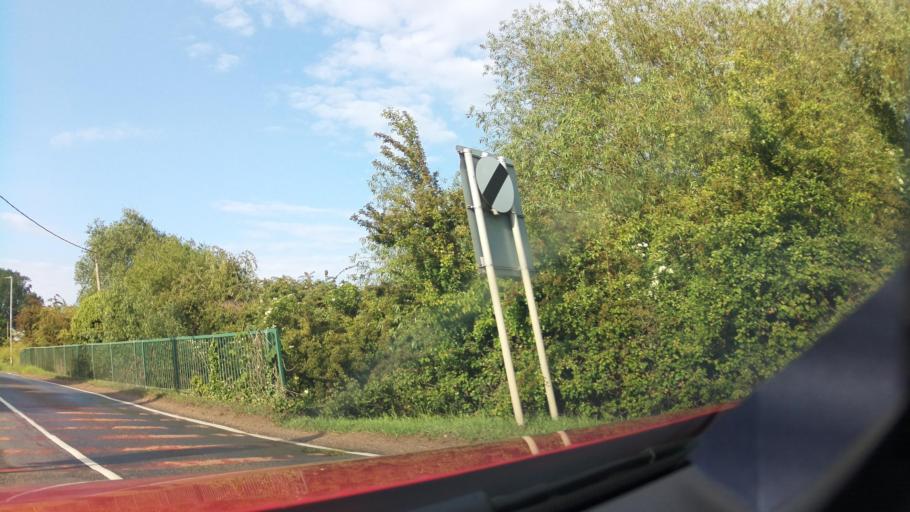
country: GB
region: England
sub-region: Lincolnshire
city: Great Gonerby
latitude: 52.9850
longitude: -0.6716
